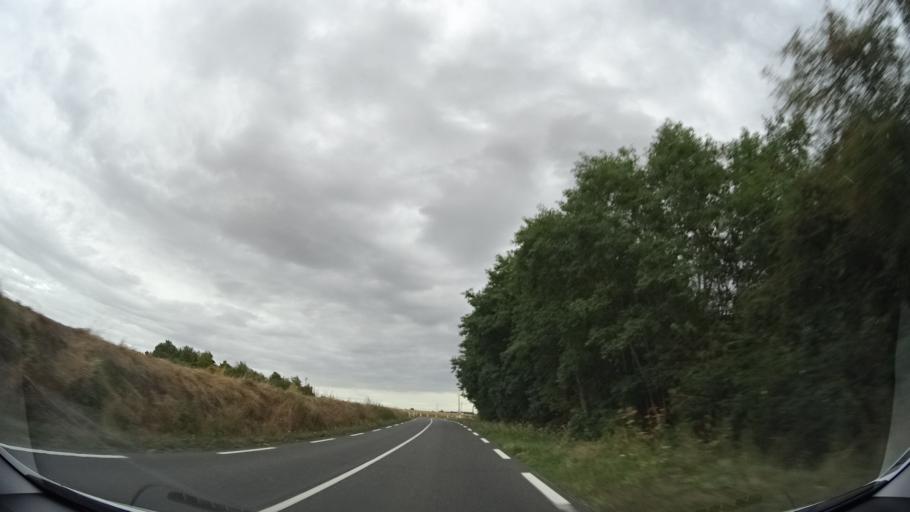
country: FR
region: Centre
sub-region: Departement du Loiret
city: Saint-Germain-des-Pres
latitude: 47.9455
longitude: 2.8719
